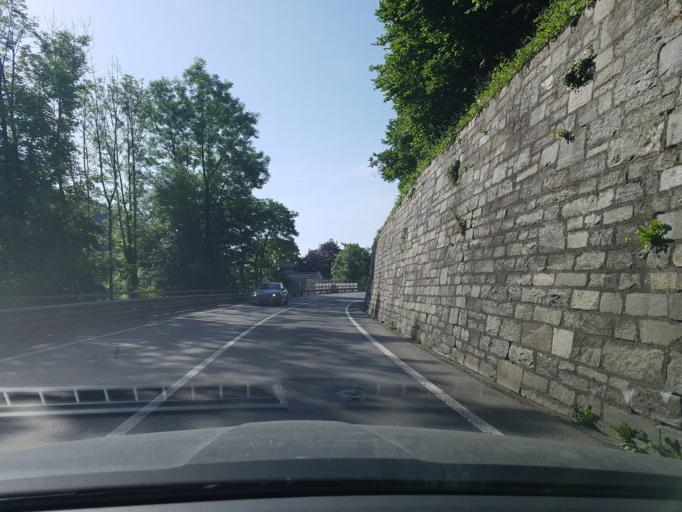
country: AT
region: Carinthia
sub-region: Politischer Bezirk Spittal an der Drau
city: Spittal an der Drau
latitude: 46.8019
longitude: 13.4972
